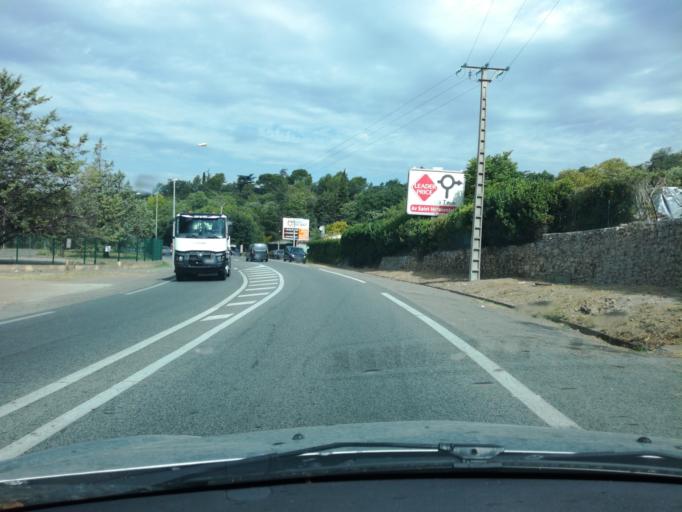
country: FR
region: Provence-Alpes-Cote d'Azur
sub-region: Departement du Var
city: Draguignan
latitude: 43.5261
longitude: 6.4596
